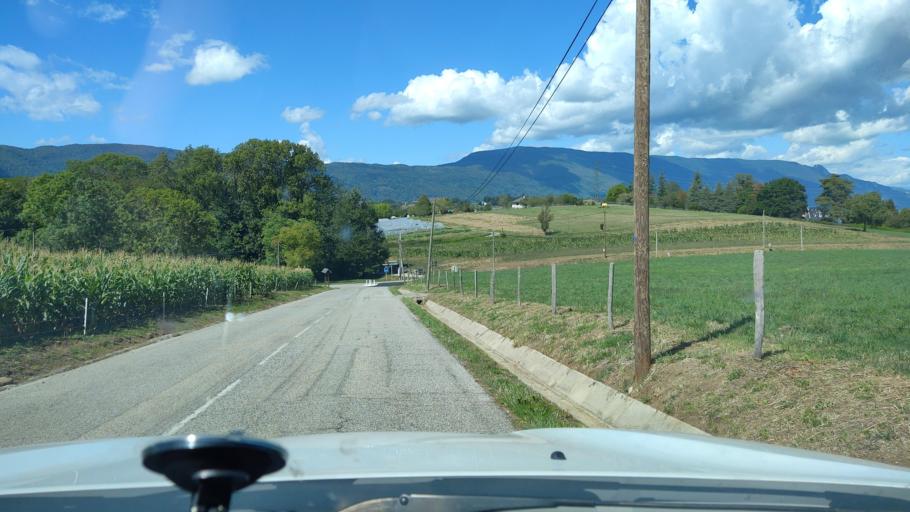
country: FR
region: Rhone-Alpes
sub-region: Departement de la Savoie
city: Jacob-Bellecombette
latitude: 45.5476
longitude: 5.9016
